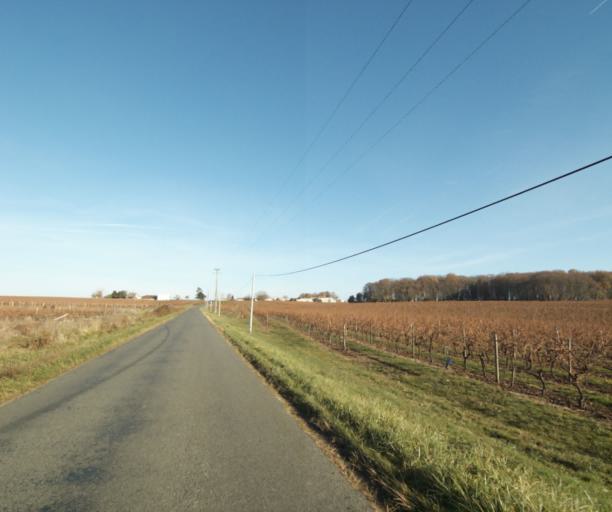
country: FR
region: Poitou-Charentes
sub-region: Departement de la Charente-Maritime
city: Cherac
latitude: 45.7339
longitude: -0.4515
